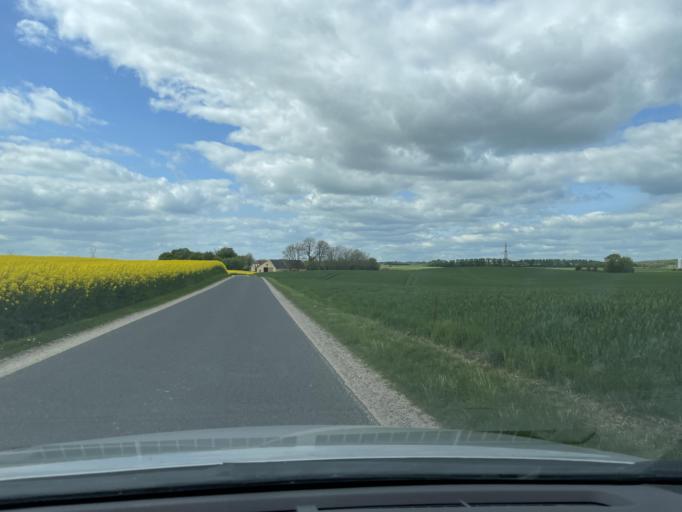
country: DK
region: Central Jutland
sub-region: Skanderborg Kommune
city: Skanderborg
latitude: 55.9209
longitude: 9.9644
